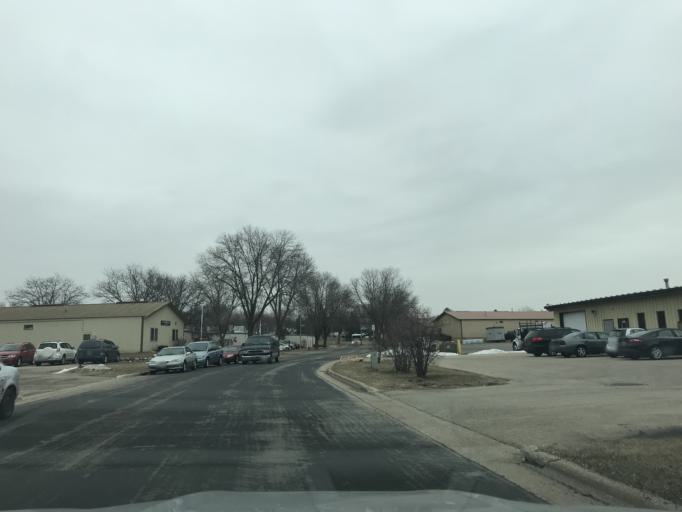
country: US
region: Wisconsin
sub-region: Dane County
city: Monona
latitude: 43.0883
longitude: -89.3106
